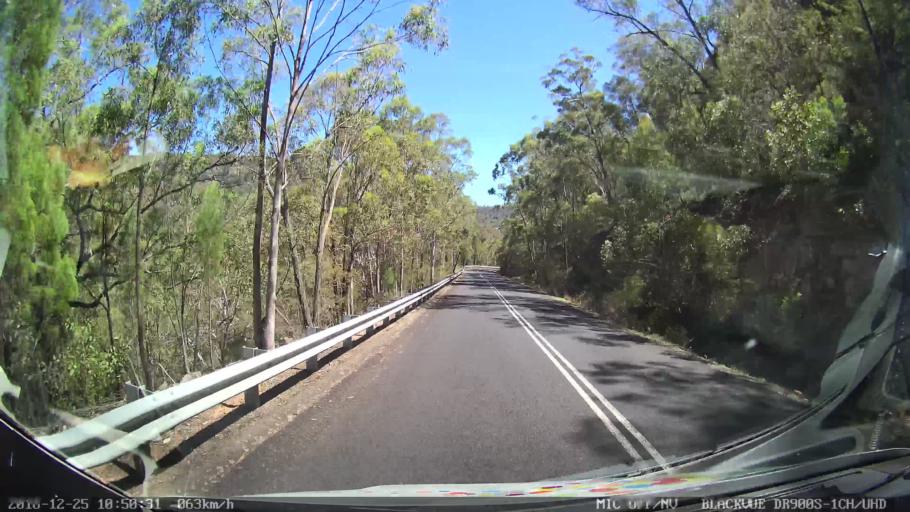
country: AU
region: New South Wales
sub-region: Upper Hunter Shire
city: Merriwa
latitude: -32.4453
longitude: 150.2679
